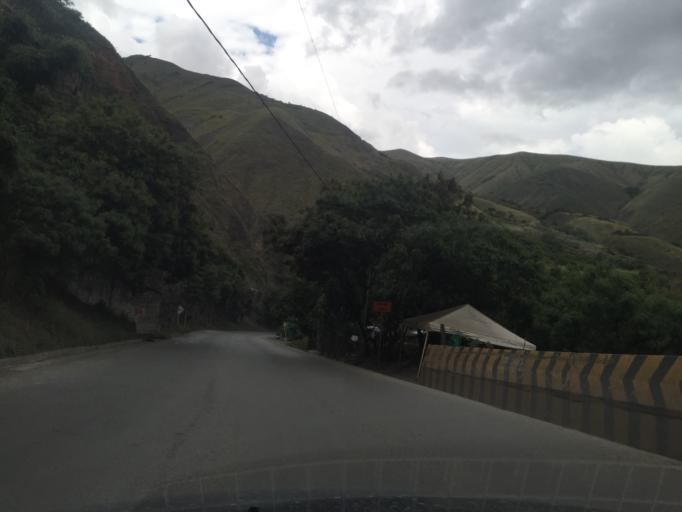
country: CO
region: Valle del Cauca
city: Dagua
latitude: 3.7677
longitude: -76.6741
